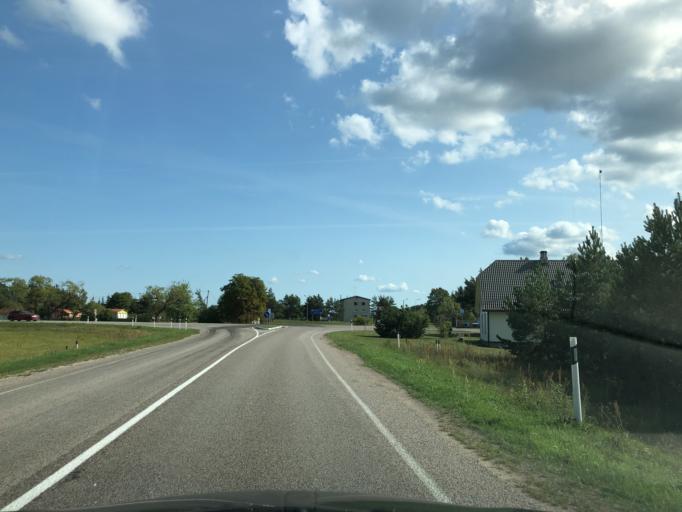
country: EE
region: Hiiumaa
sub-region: Kaerdla linn
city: Kardla
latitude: 58.7061
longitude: 22.5964
